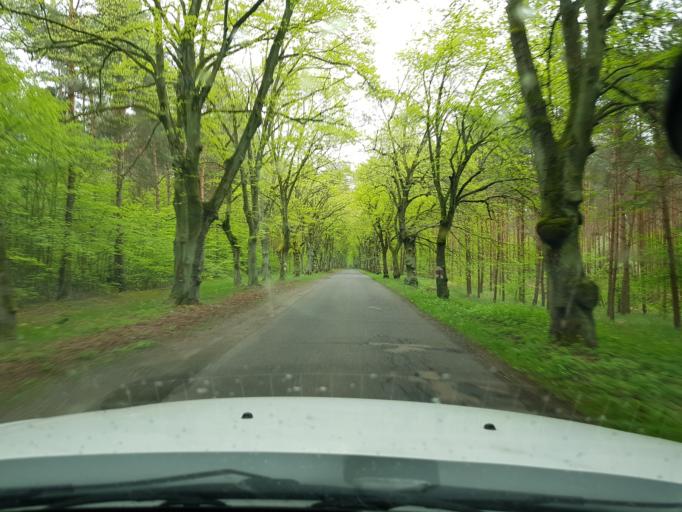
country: PL
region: West Pomeranian Voivodeship
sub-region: Powiat mysliborski
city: Debno
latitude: 52.6989
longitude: 14.6689
